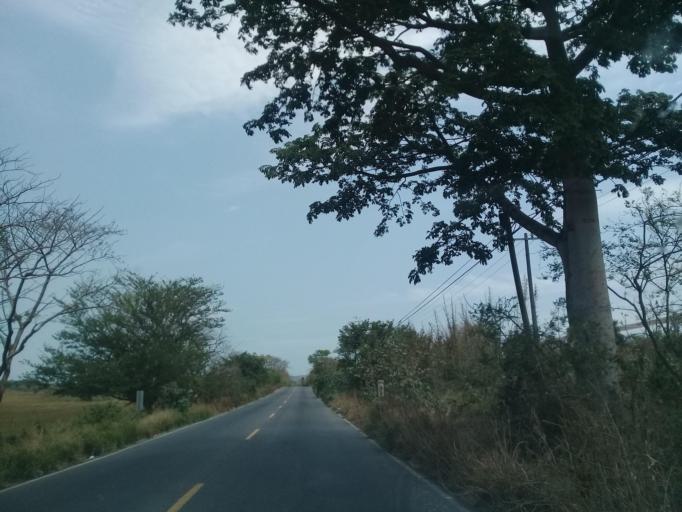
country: MX
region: Veracruz
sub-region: Veracruz
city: Delfino Victoria (Santa Fe)
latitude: 19.1638
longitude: -96.2870
